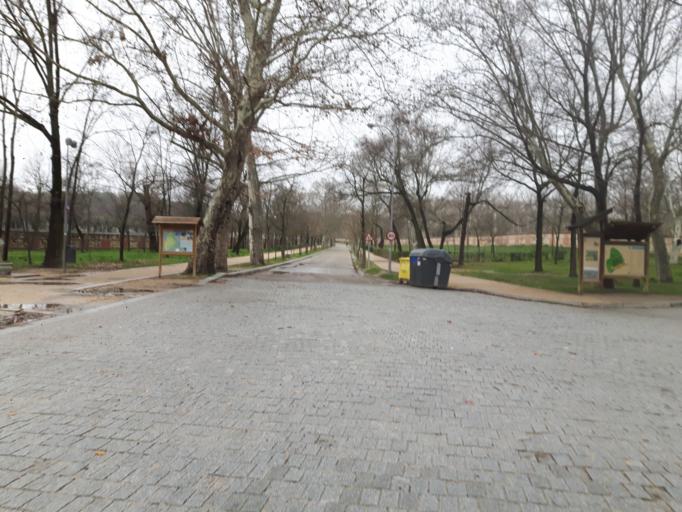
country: ES
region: Madrid
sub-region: Provincia de Madrid
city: Moncloa-Aravaca
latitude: 40.4186
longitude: -3.7239
